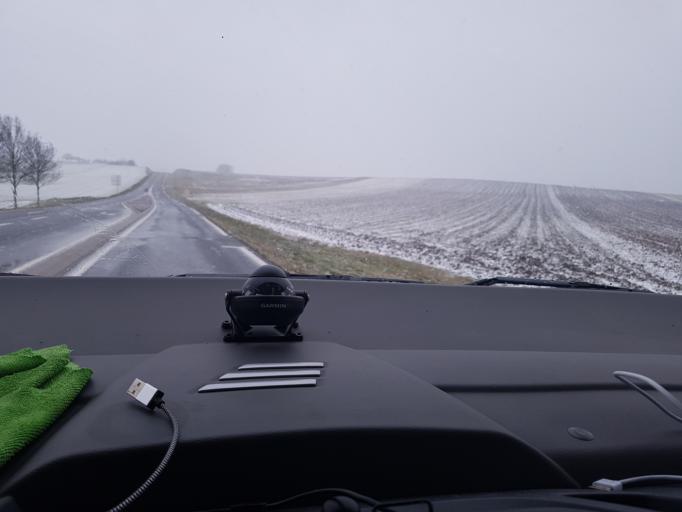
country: FR
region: Lorraine
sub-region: Departement de la Moselle
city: Dieuze
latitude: 48.7282
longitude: 6.7050
